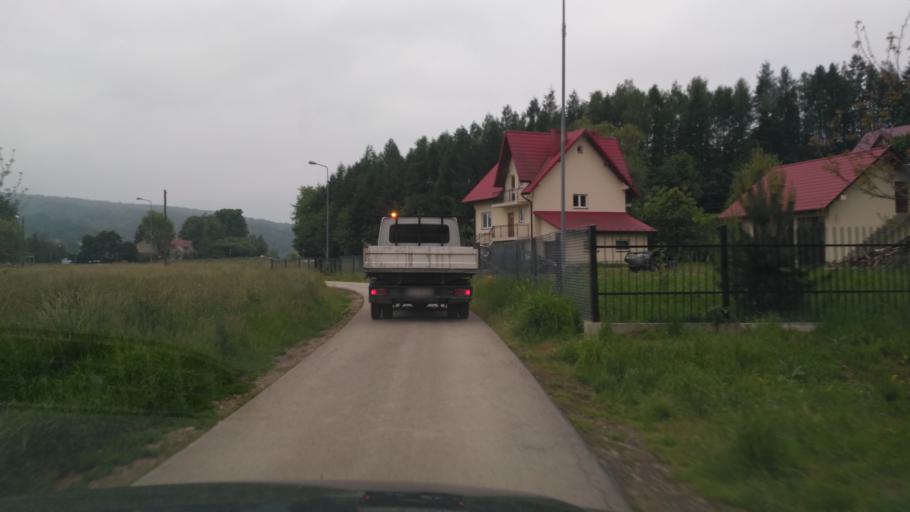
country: PL
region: Subcarpathian Voivodeship
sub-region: Powiat rzeszowski
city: Dynow
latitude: 49.8091
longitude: 22.2371
